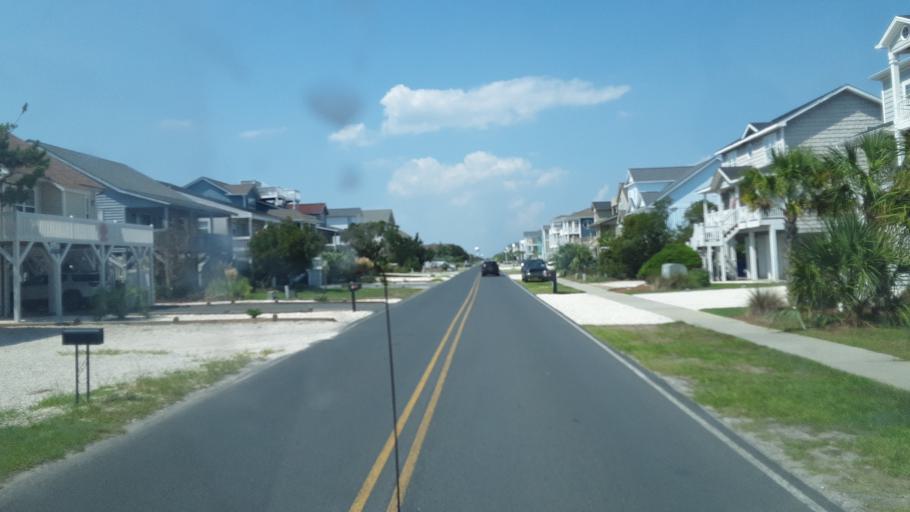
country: US
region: North Carolina
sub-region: Brunswick County
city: Shallotte
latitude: 33.8948
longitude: -78.4113
